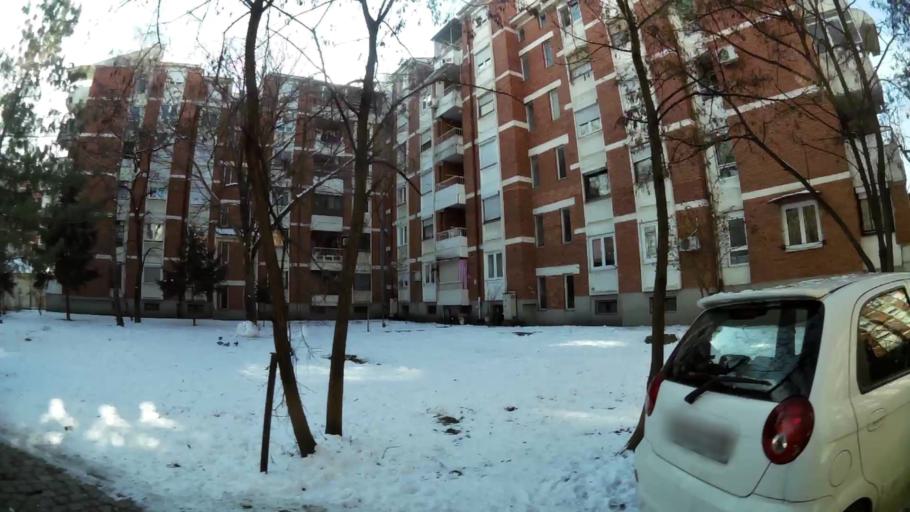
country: MK
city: Krushopek
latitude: 42.0089
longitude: 21.3600
